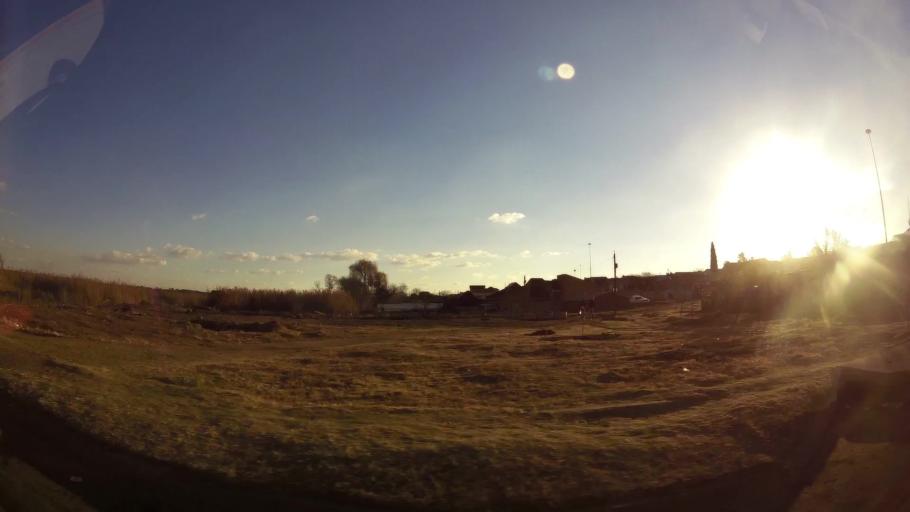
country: ZA
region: Mpumalanga
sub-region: Nkangala District Municipality
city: Witbank
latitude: -25.8763
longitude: 29.1825
